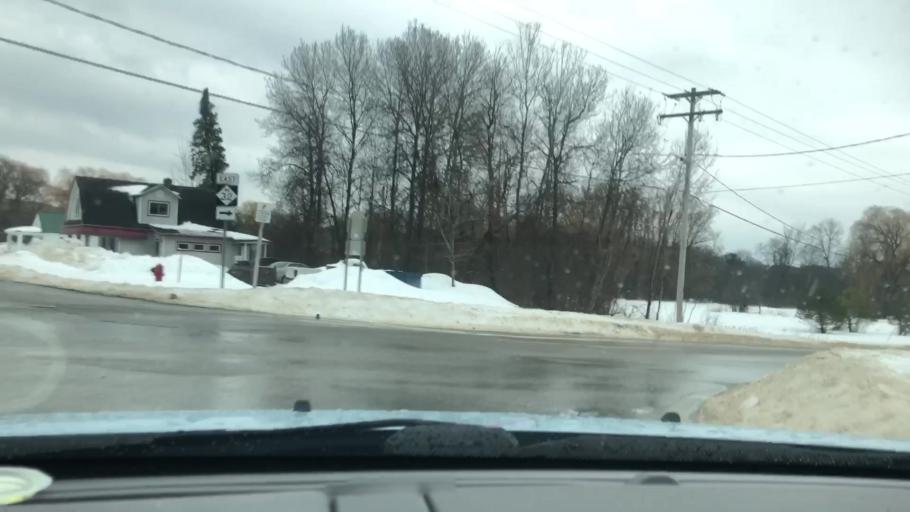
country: US
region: Michigan
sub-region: Charlevoix County
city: East Jordan
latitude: 45.1522
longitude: -85.1192
